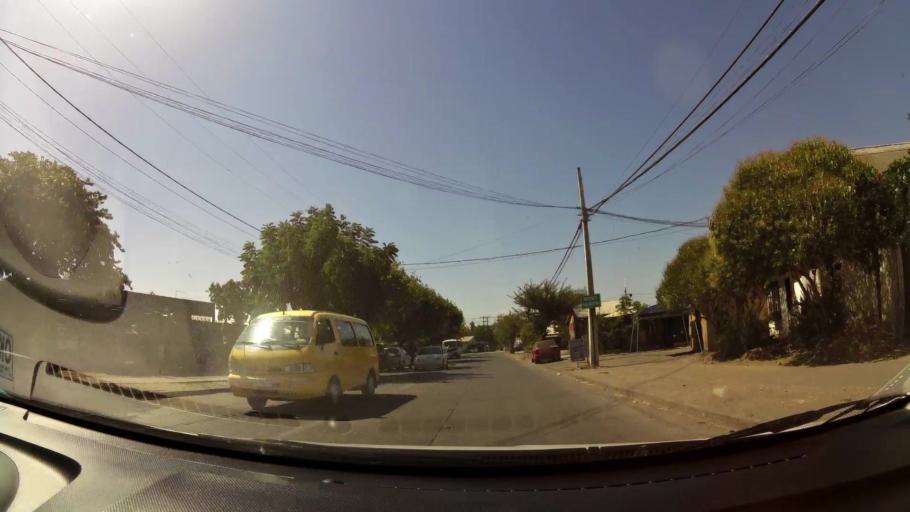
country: CL
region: Maule
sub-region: Provincia de Talca
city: Talca
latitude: -35.4410
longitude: -71.6628
